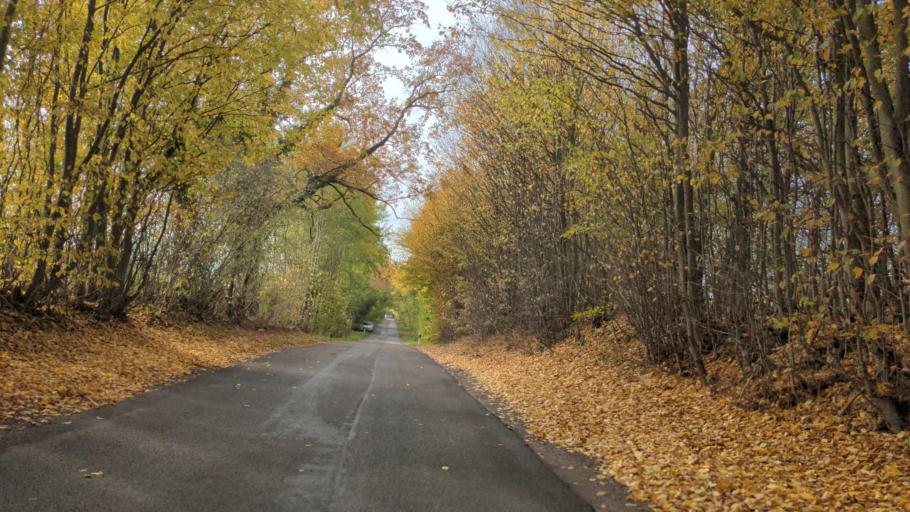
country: DE
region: Mecklenburg-Vorpommern
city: Selmsdorf
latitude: 53.9147
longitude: 10.8328
